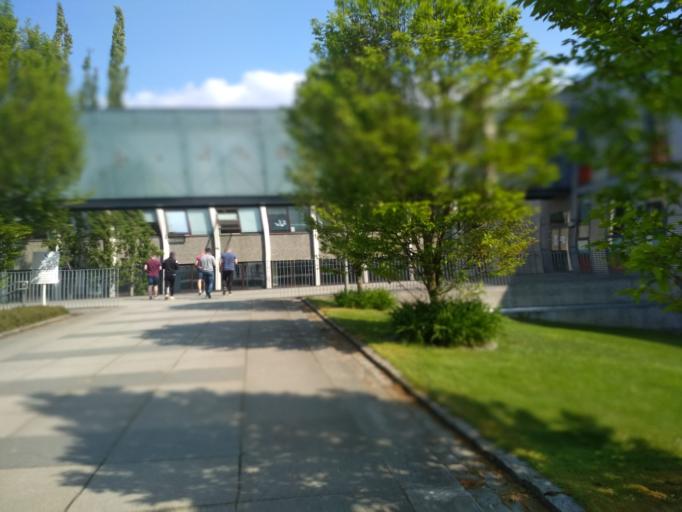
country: NO
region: Rogaland
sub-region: Stavanger
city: Stavanger
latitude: 58.9377
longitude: 5.6987
